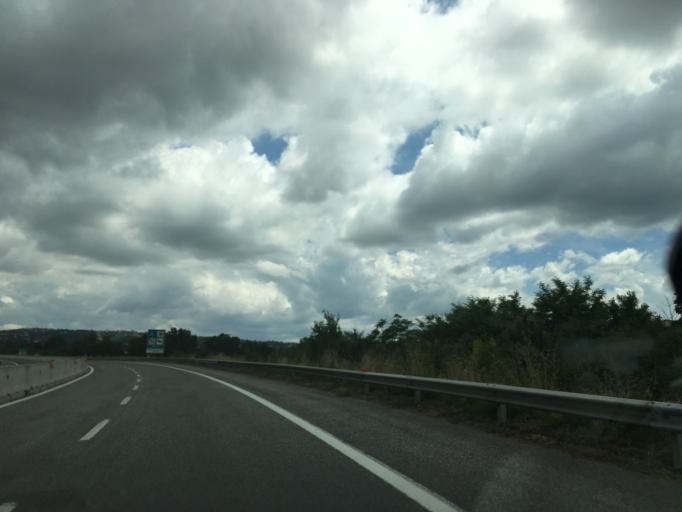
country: IT
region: Campania
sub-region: Provincia di Avellino
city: Passo di Mirabella-Pianopantano
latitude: 41.0642
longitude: 15.0071
